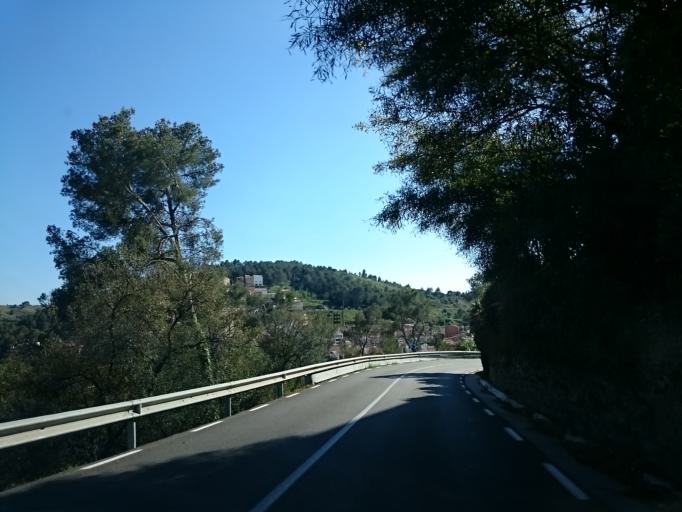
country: ES
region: Catalonia
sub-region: Provincia de Barcelona
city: Torrelles de Llobregat
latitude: 41.3387
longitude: 2.0000
